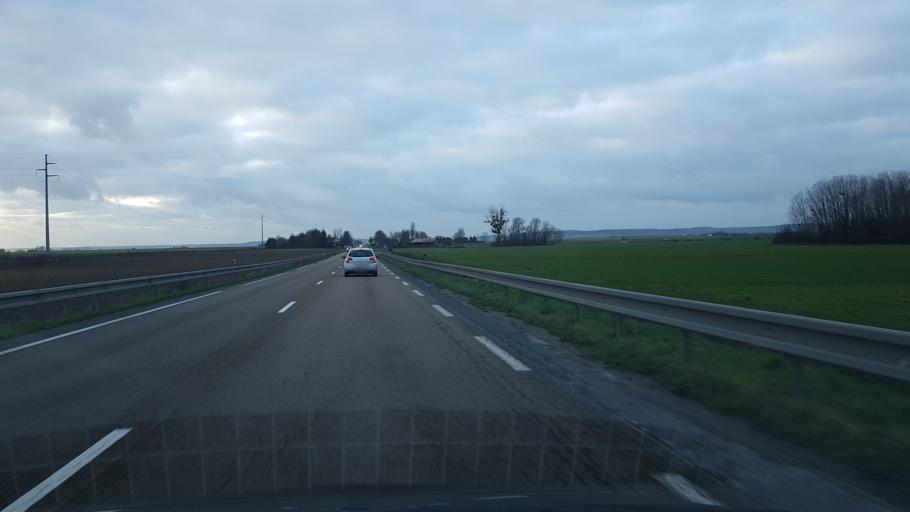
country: FR
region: Champagne-Ardenne
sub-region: Departement de la Marne
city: Connantre
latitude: 48.7264
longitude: 3.8487
